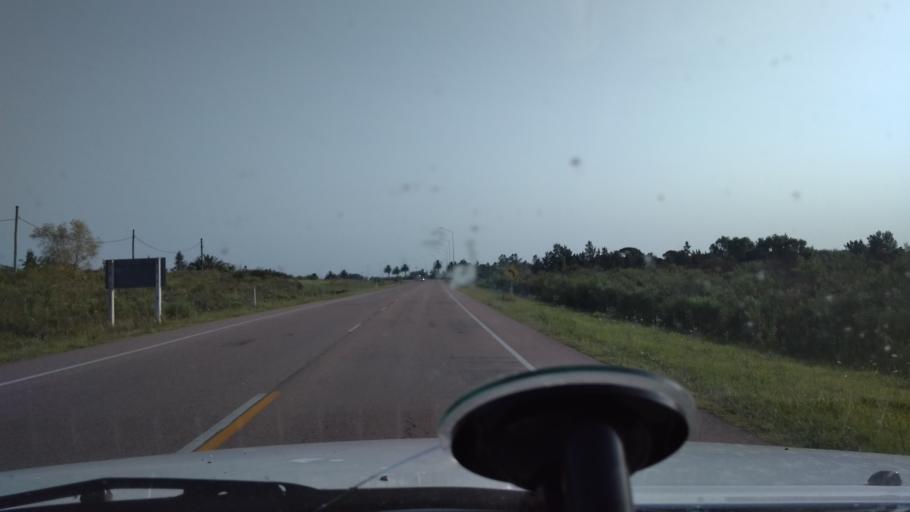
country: UY
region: Canelones
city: Sauce
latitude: -34.6601
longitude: -56.0563
